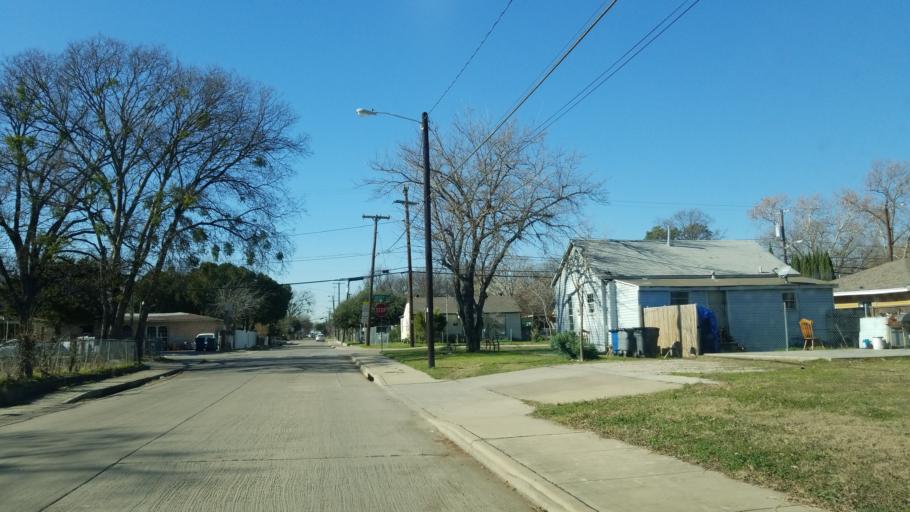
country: US
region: Texas
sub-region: Dallas County
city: Cockrell Hill
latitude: 32.7562
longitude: -96.9109
